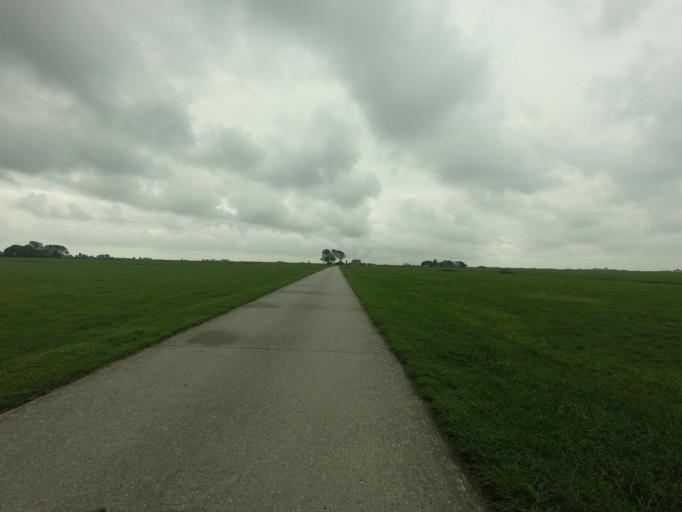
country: NL
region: Friesland
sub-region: Sudwest Fryslan
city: Bolsward
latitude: 53.0068
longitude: 5.5207
